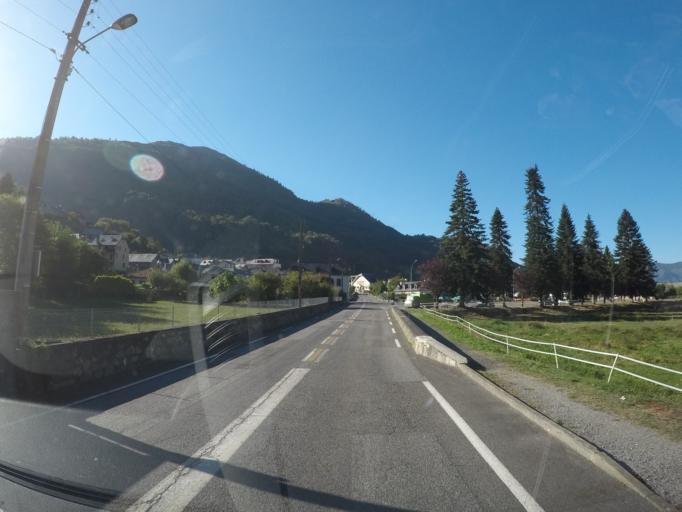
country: FR
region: Midi-Pyrenees
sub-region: Departement des Hautes-Pyrenees
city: Pierrefitte-Nestalas
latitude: 42.9551
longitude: -0.0718
